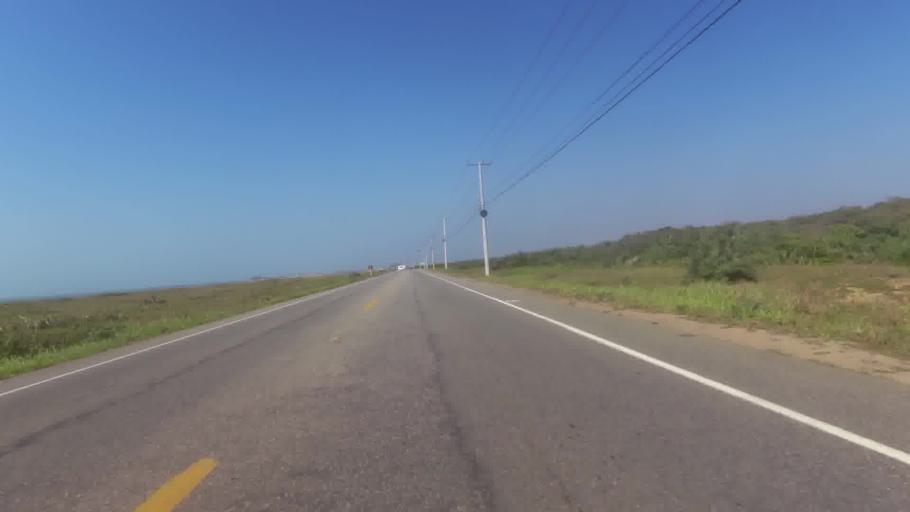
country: BR
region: Espirito Santo
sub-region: Itapemirim
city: Itapemirim
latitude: -20.9742
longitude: -40.8115
